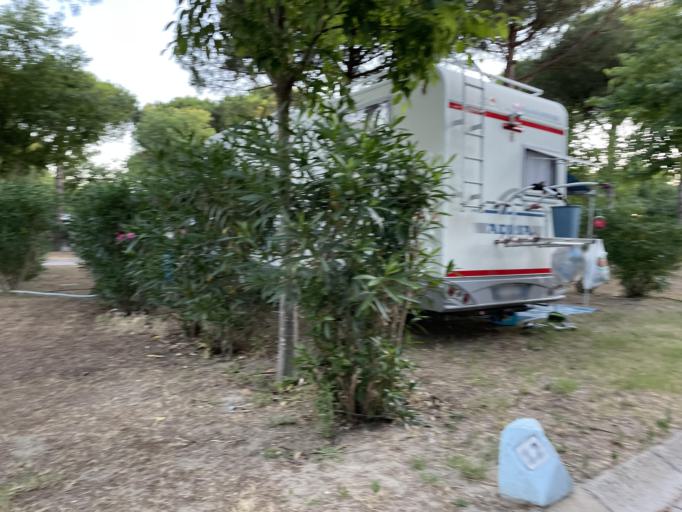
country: IT
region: Emilia-Romagna
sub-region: Provincia di Ferrara
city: San Giuseppe
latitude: 44.7322
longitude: 12.2306
